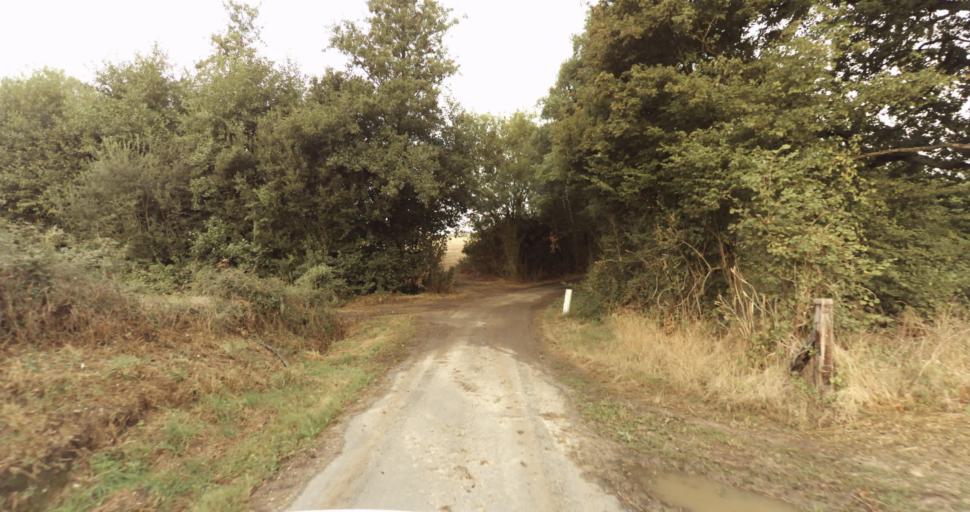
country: FR
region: Lower Normandy
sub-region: Departement de l'Orne
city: Trun
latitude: 48.8987
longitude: 0.0925
